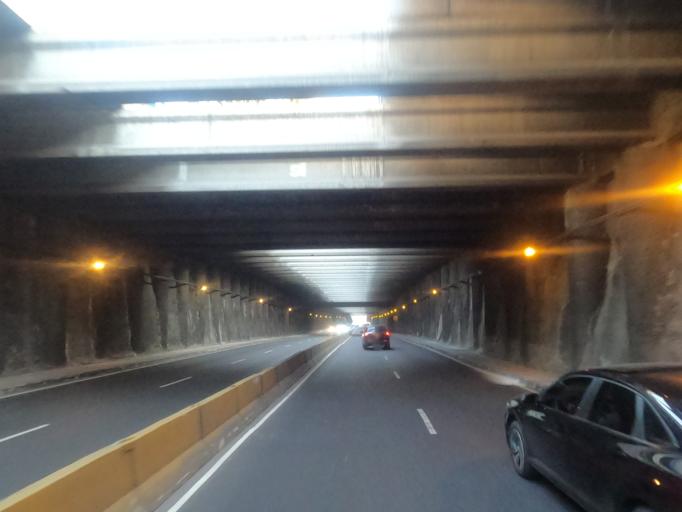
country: MX
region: Mexico City
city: Alvaro Obregon
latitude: 19.3579
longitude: -99.2066
